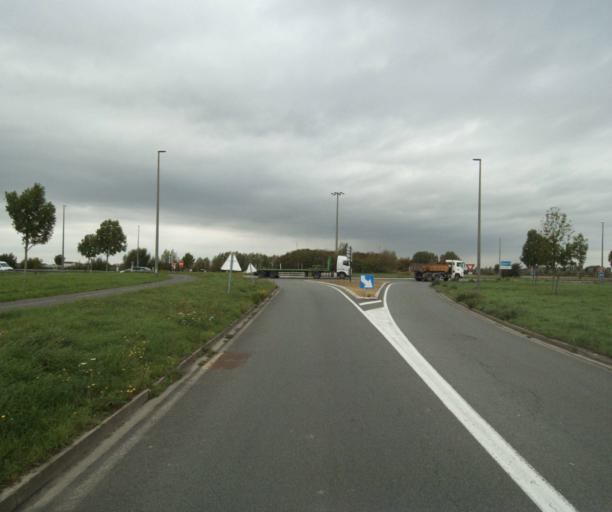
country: FR
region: Nord-Pas-de-Calais
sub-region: Departement du Nord
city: Herlies
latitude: 50.5685
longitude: 2.8558
